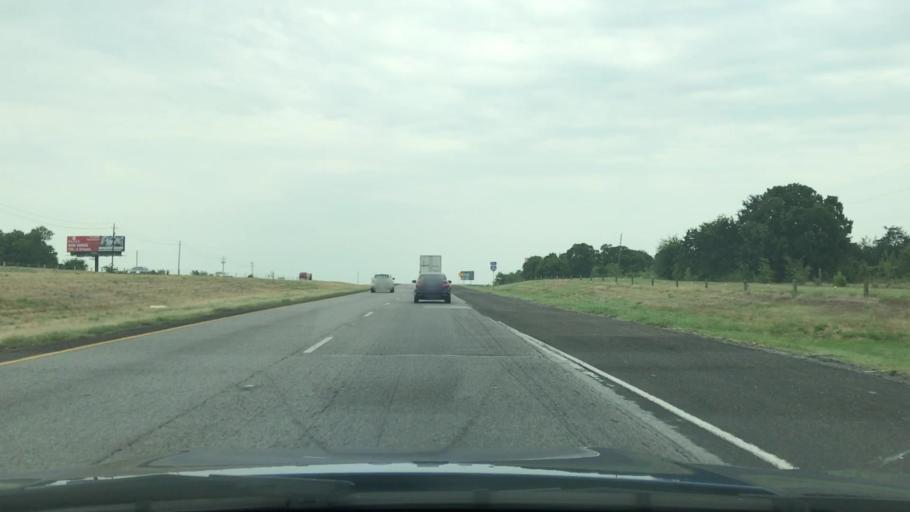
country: US
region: Texas
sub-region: Kaufman County
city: Terrell
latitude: 32.7094
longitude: -96.2939
